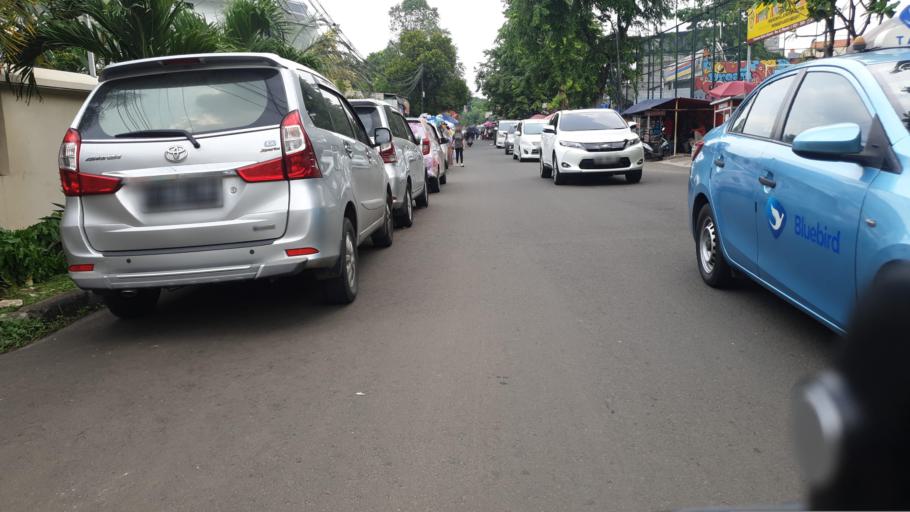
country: ID
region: West Java
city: Ciputat
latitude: -6.1959
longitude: 106.7515
